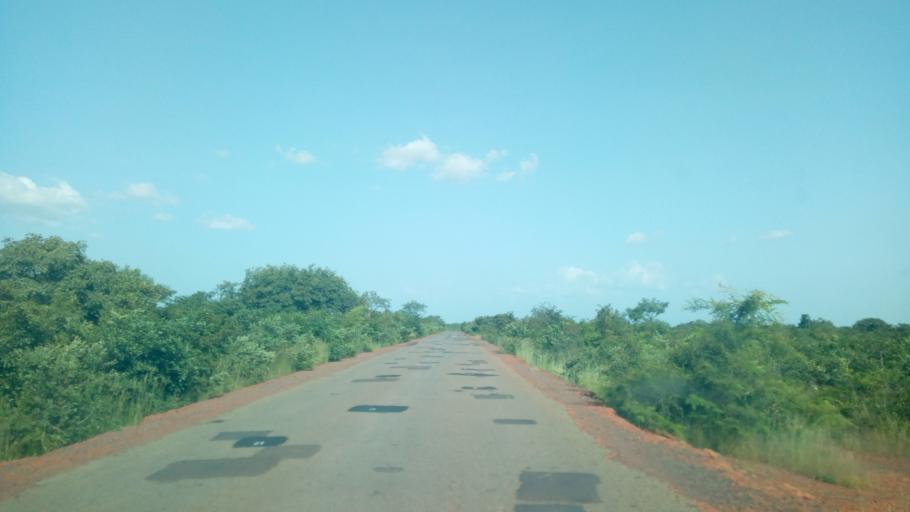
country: ML
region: Sikasso
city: Yorosso
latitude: 12.2122
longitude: -4.9047
